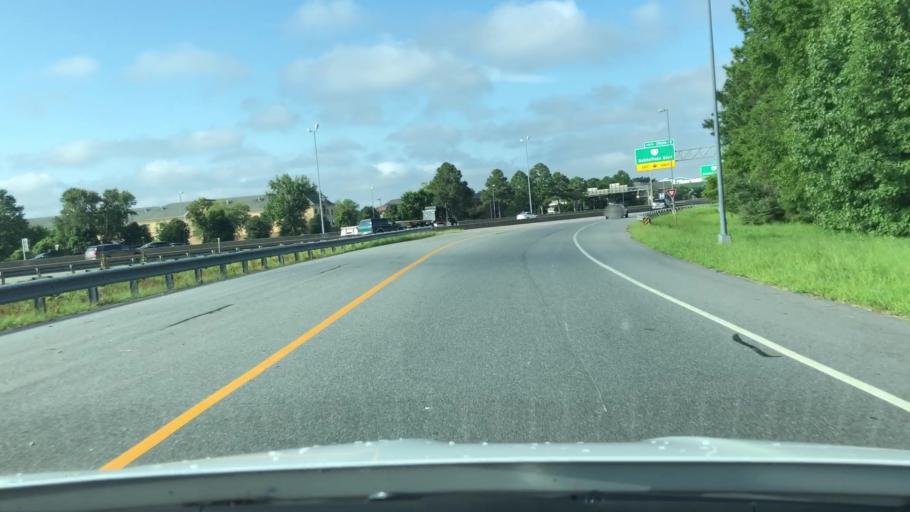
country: US
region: Virginia
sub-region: City of Chesapeake
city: Chesapeake
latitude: 36.7835
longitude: -76.2373
